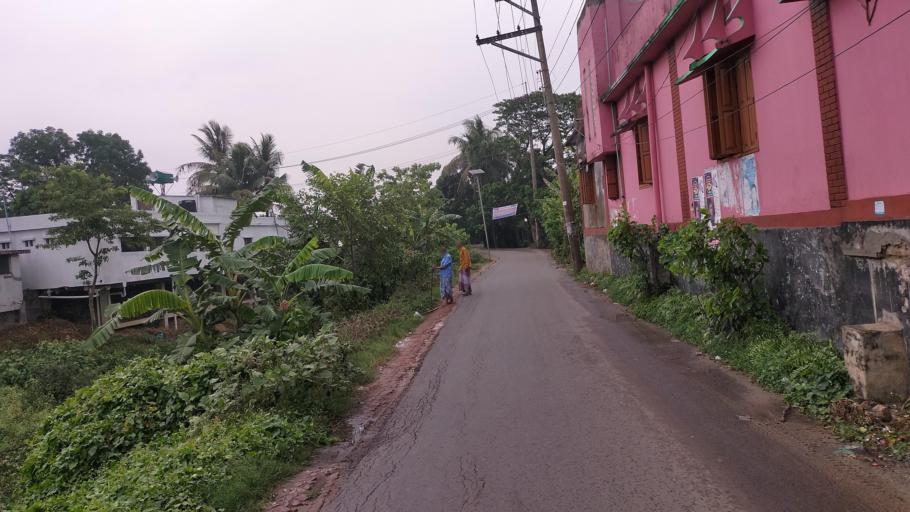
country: BD
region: Dhaka
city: Azimpur
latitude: 23.6773
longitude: 90.3484
